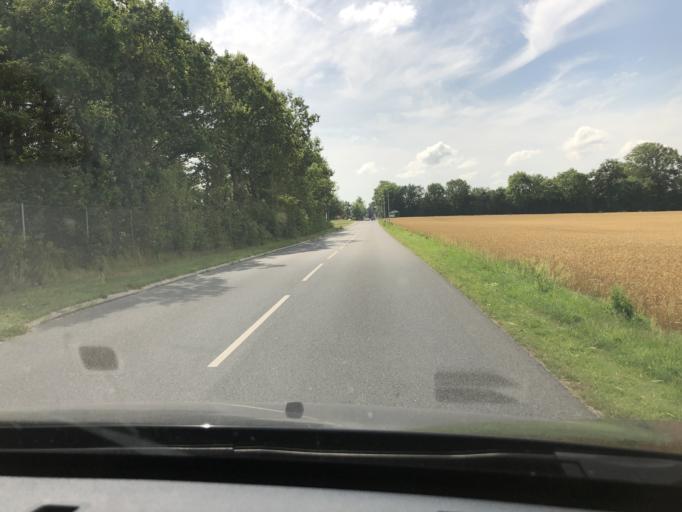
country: DK
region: Central Jutland
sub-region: Norddjurs Kommune
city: Allingabro
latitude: 56.5101
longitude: 10.3325
